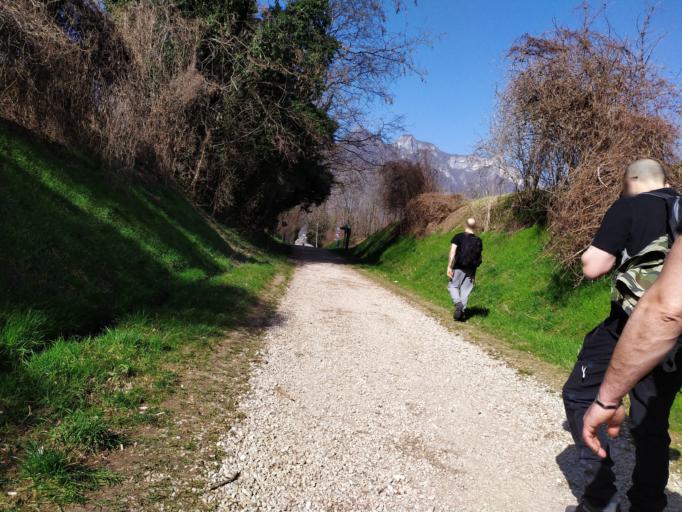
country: IT
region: Veneto
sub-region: Provincia di Vicenza
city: Velo
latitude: 45.7929
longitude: 11.3740
